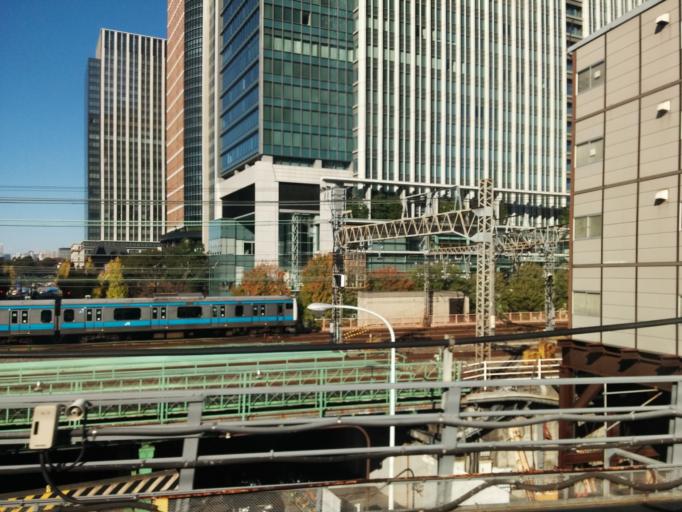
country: JP
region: Tokyo
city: Tokyo
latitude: 35.6774
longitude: 139.7658
